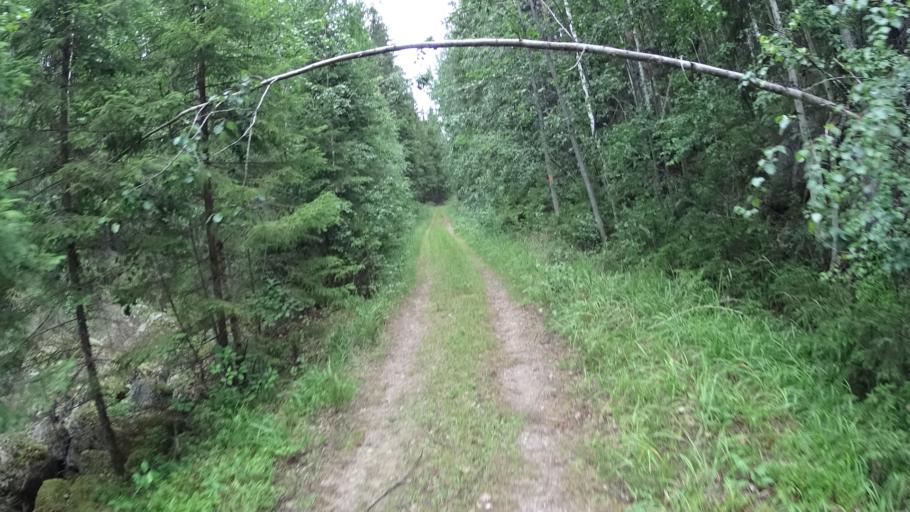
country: FI
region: Southern Savonia
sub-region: Mikkeli
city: Maentyharju
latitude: 61.1857
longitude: 26.8288
